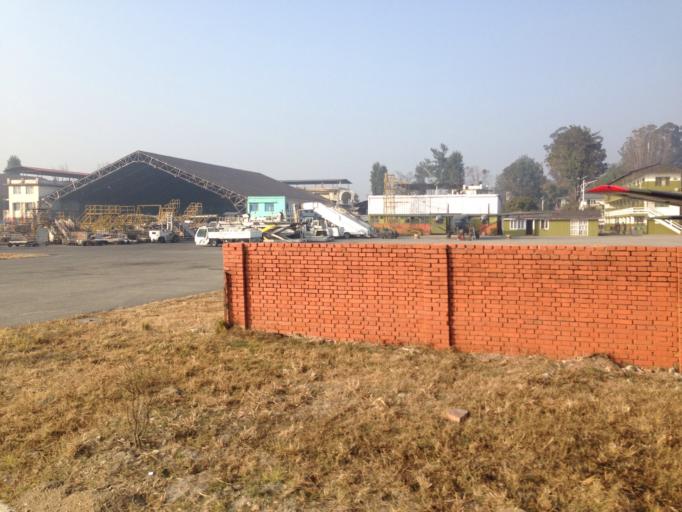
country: NP
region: Central Region
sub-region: Bagmati Zone
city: Kathmandu
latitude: 27.7044
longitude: 85.3598
